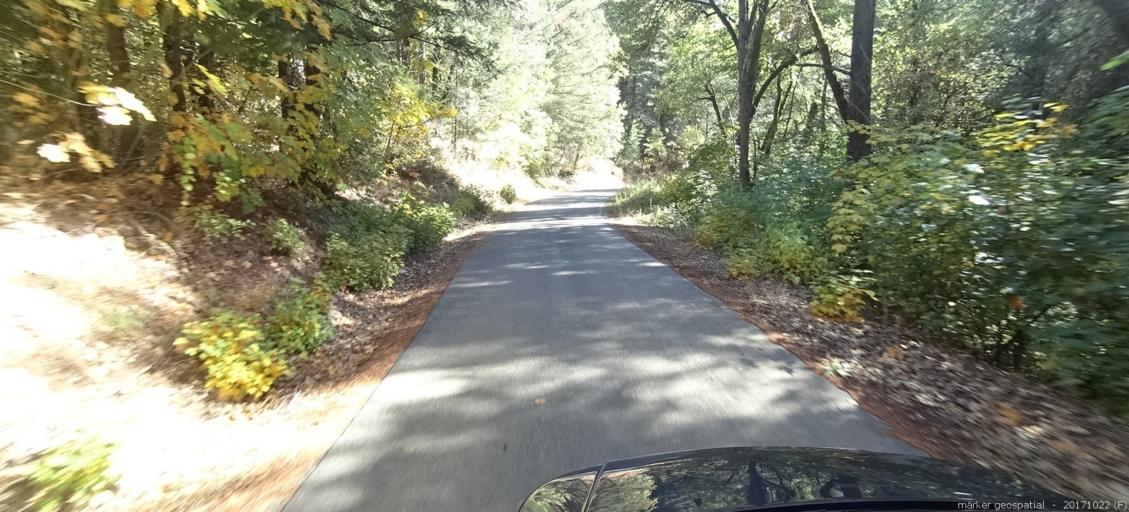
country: US
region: California
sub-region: Shasta County
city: Central Valley (historical)
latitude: 40.9303
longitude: -122.4893
